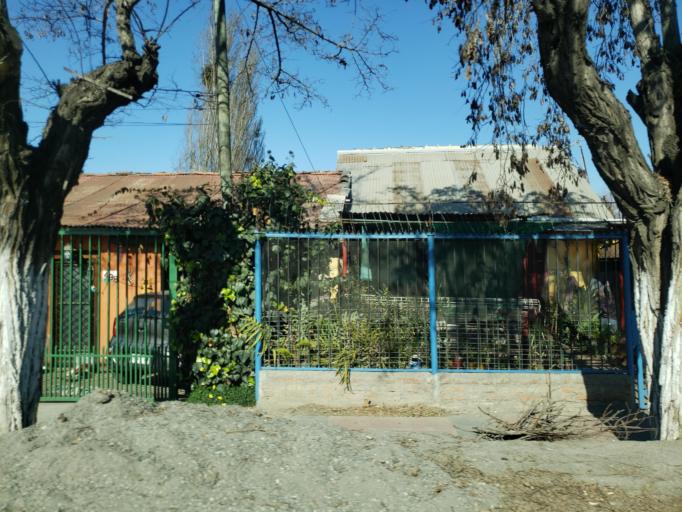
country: CL
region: Santiago Metropolitan
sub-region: Provincia de Talagante
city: El Monte
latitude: -33.6821
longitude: -70.9839
